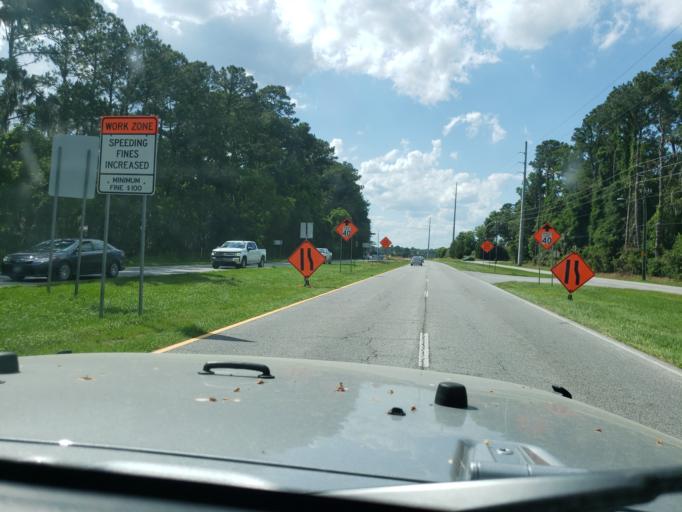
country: US
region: Georgia
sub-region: Chatham County
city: Whitemarsh Island
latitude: 32.0552
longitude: -81.0172
